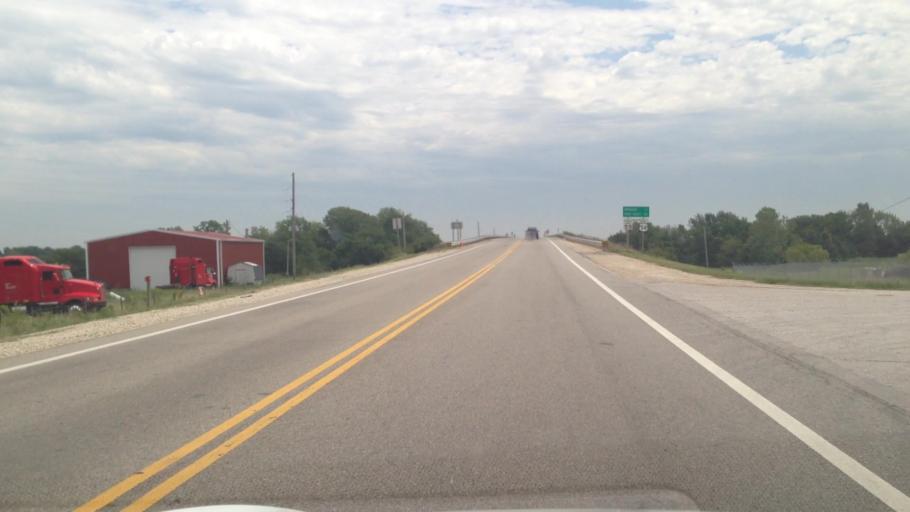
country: US
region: Kansas
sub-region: Allen County
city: Iola
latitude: 37.9216
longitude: -95.1690
